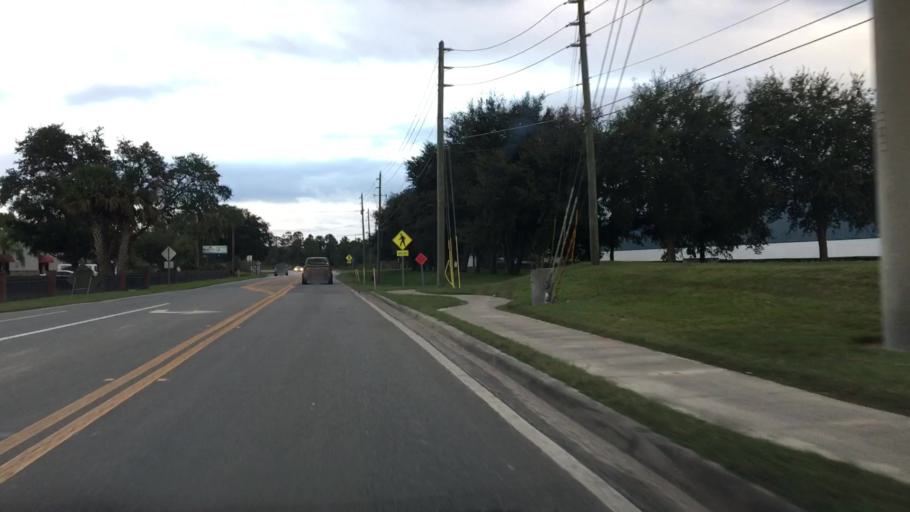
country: US
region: Florida
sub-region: Volusia County
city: DeBary
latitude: 28.8296
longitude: -81.3294
